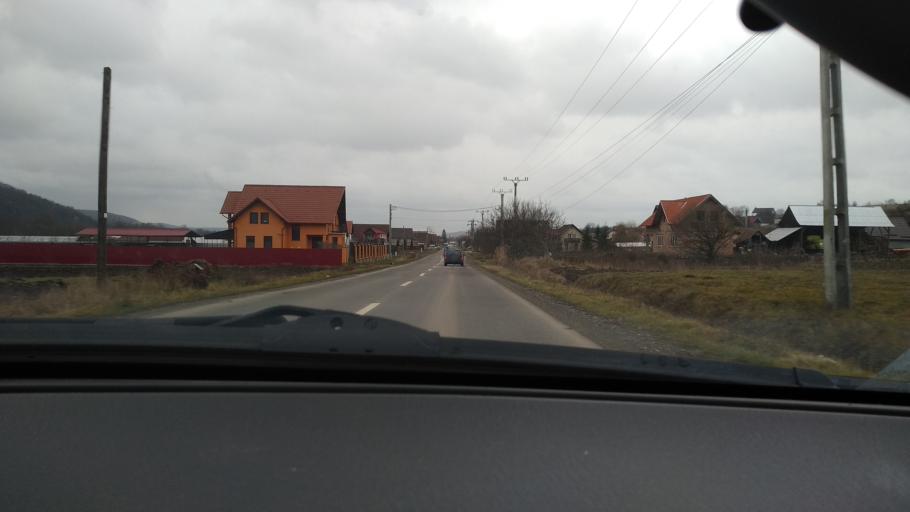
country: RO
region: Mures
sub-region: Comuna Miercurea Nirajului
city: Miercurea Nirajului
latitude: 46.5442
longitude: 24.8301
